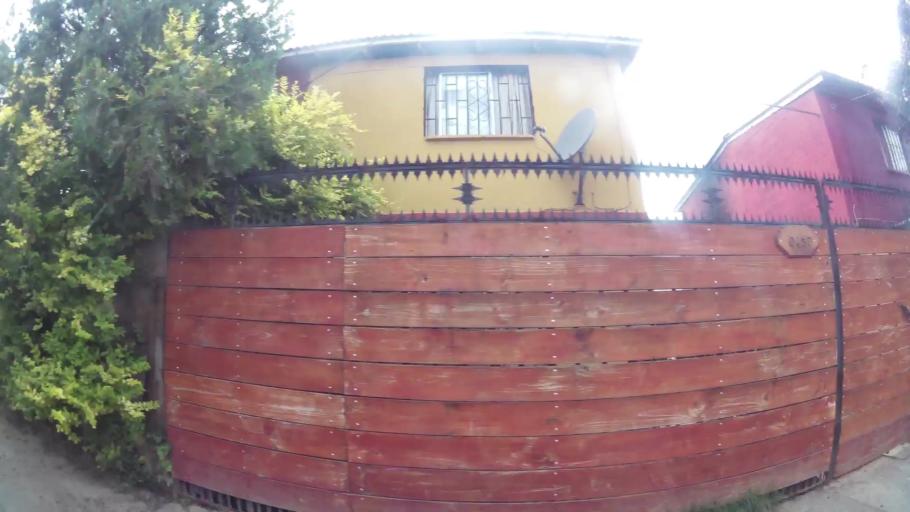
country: CL
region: Santiago Metropolitan
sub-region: Provincia de Cordillera
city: Puente Alto
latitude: -33.6228
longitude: -70.6110
